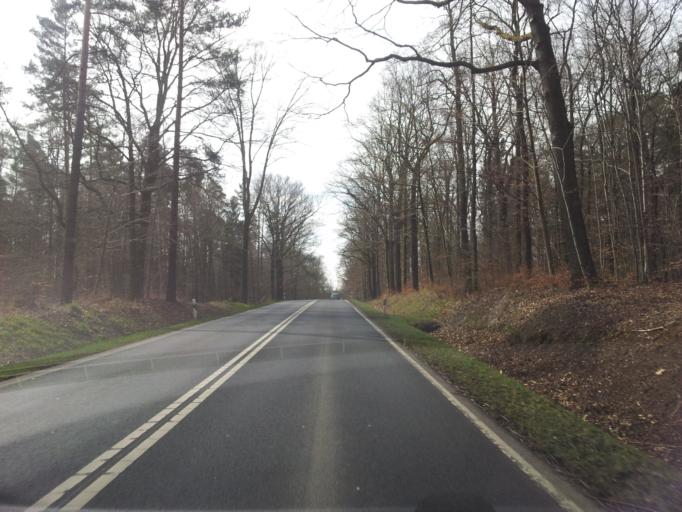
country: DE
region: Saxony
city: Ottendorf-Okrilla
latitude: 51.2155
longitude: 13.8411
